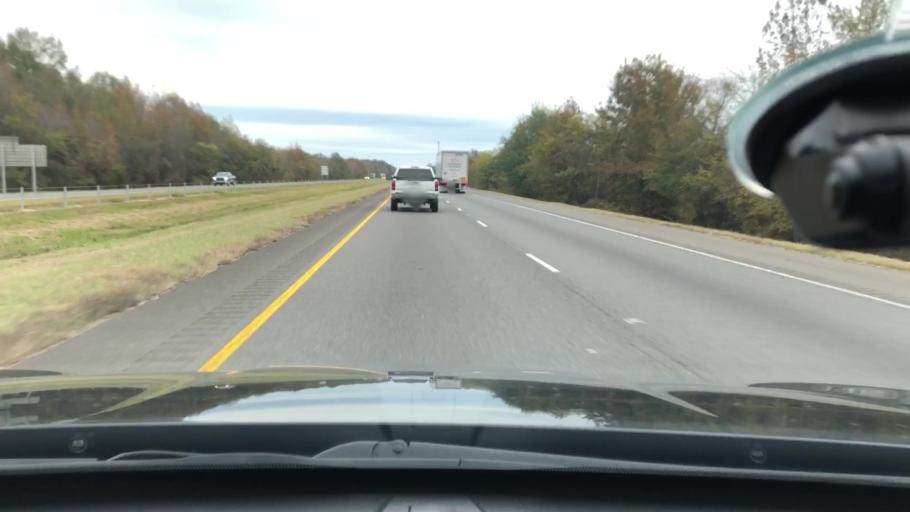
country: US
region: Arkansas
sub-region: Clark County
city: Gurdon
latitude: 34.0054
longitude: -93.1751
